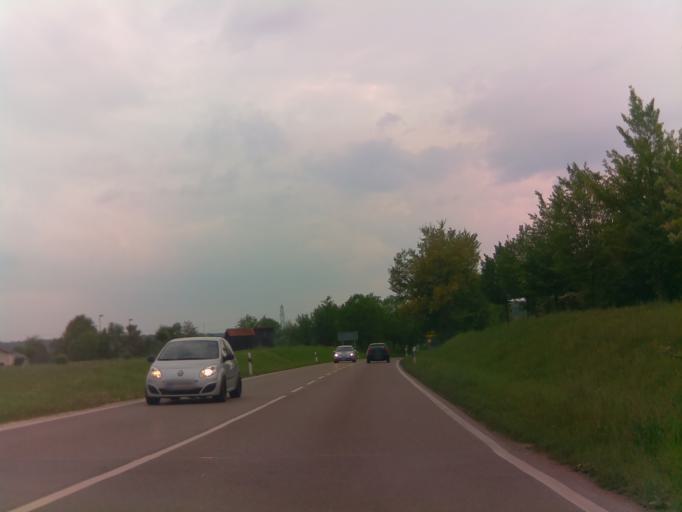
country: DE
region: Baden-Wuerttemberg
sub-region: Tuebingen Region
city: Pliezhausen
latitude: 48.5805
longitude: 9.1803
